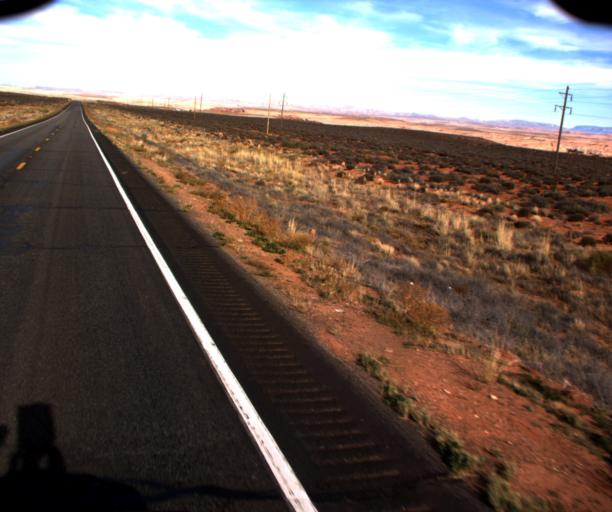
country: US
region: Arizona
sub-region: Navajo County
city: Kayenta
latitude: 36.9207
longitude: -109.7641
